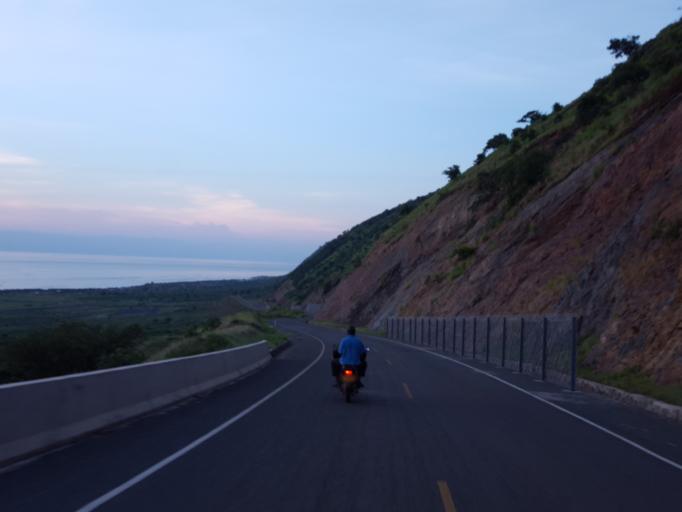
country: UG
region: Western Region
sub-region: Kibale District
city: Kagadi
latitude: 1.2412
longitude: 30.7581
